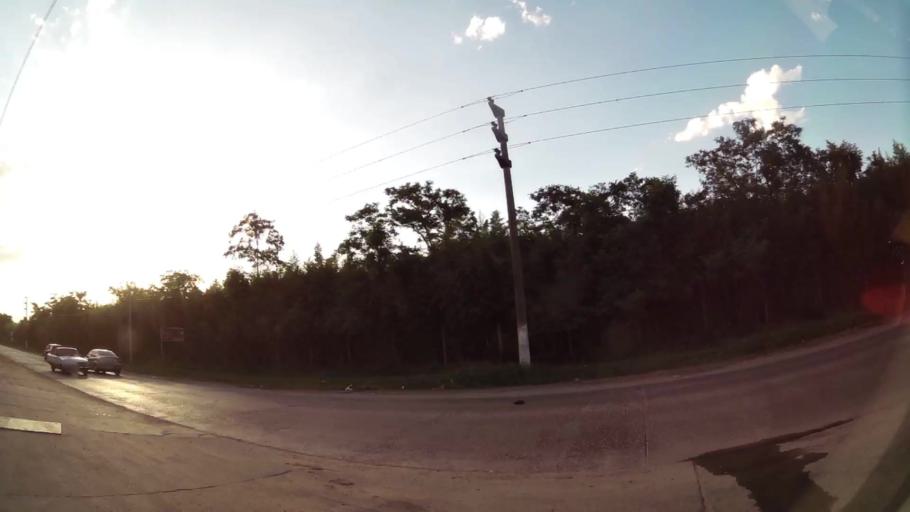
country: AR
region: Buenos Aires
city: Santa Catalina - Dique Lujan
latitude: -34.4659
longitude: -58.7484
